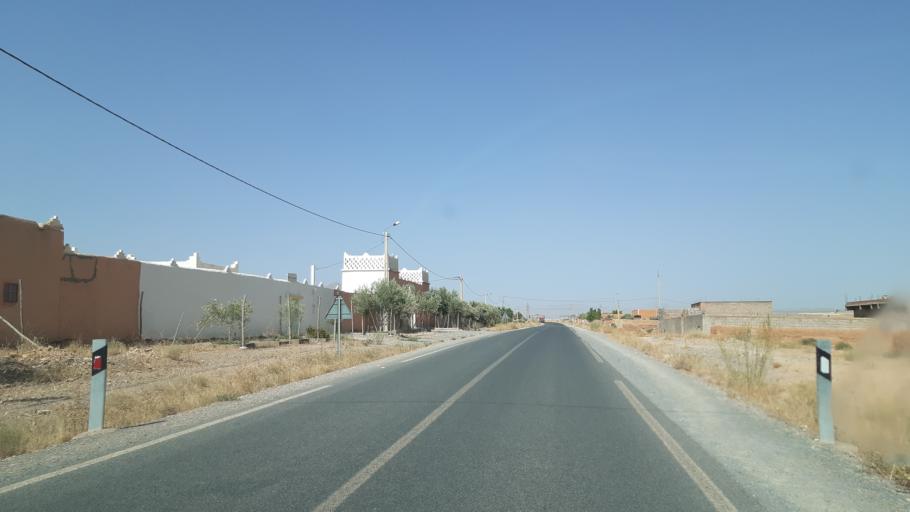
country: MA
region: Meknes-Tafilalet
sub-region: Errachidia
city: Amouguer
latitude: 32.2400
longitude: -4.6030
